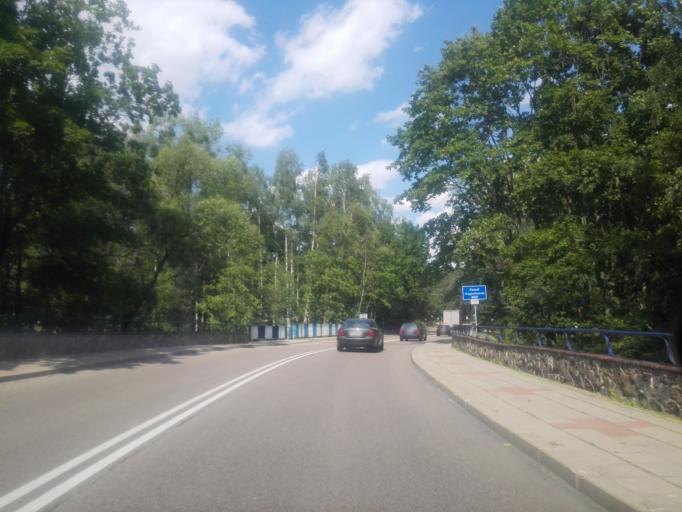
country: PL
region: Podlasie
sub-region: Powiat augustowski
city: Augustow
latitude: 53.8672
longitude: 23.0915
